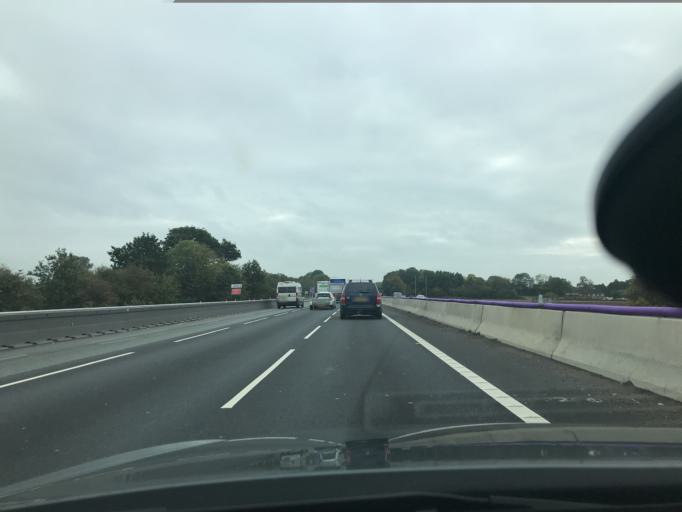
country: GB
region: England
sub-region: Cheshire East
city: Peover Superior
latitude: 53.2473
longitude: -2.4016
